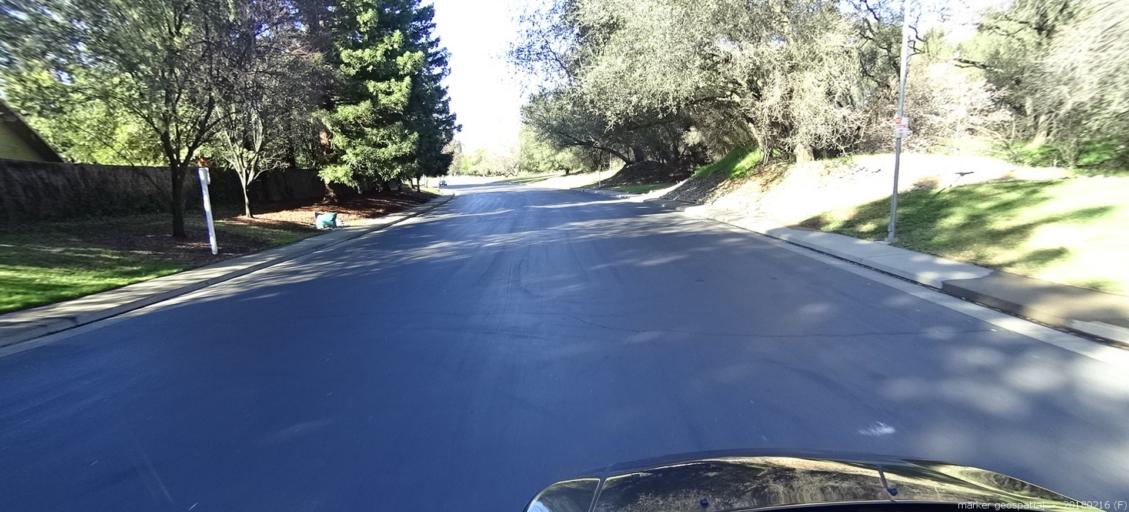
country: US
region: California
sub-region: Sacramento County
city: Gold River
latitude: 38.6311
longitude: -121.2497
